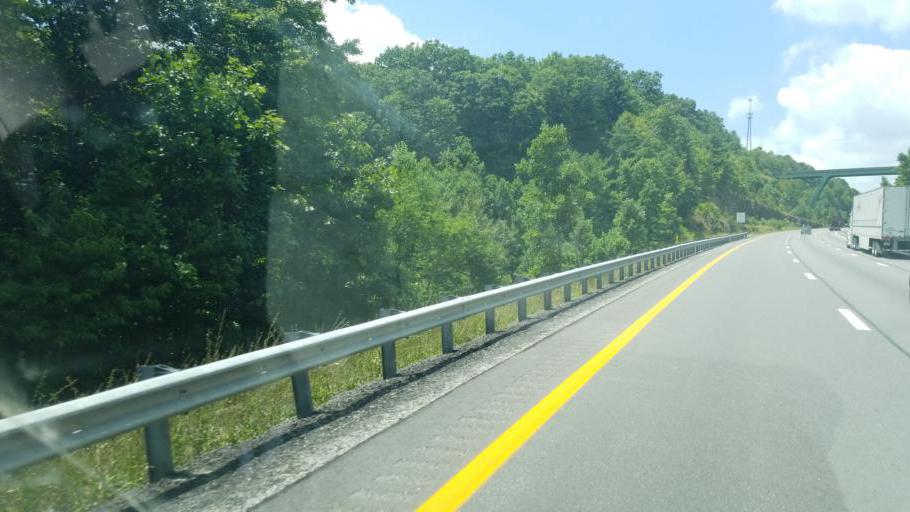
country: US
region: West Virginia
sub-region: Raleigh County
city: Beaver
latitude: 37.7226
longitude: -81.1782
